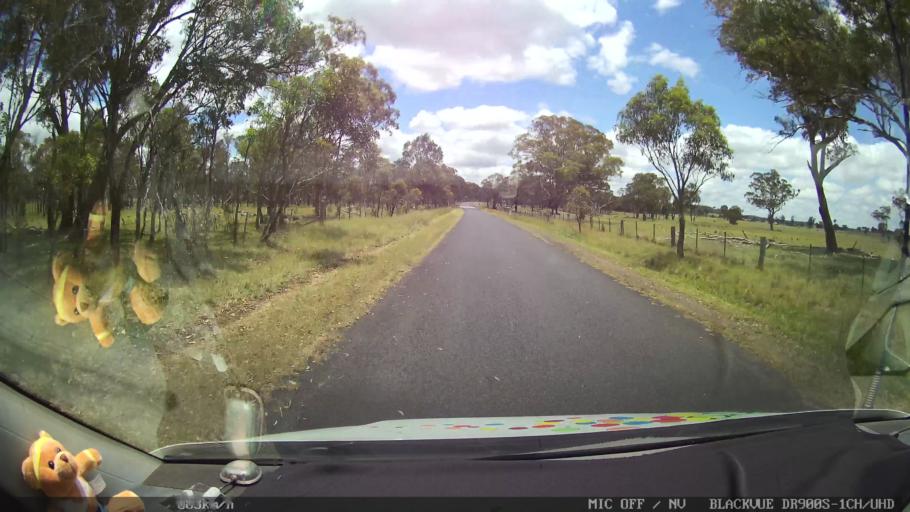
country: AU
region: New South Wales
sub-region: Glen Innes Severn
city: Glen Innes
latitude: -29.4202
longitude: 151.7280
